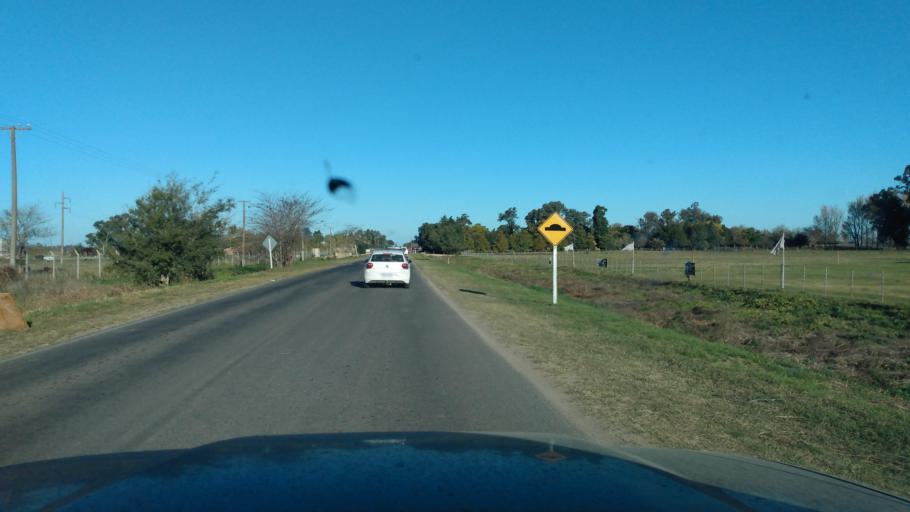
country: AR
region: Buenos Aires
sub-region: Partido de Lujan
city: Lujan
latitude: -34.5059
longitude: -59.1871
